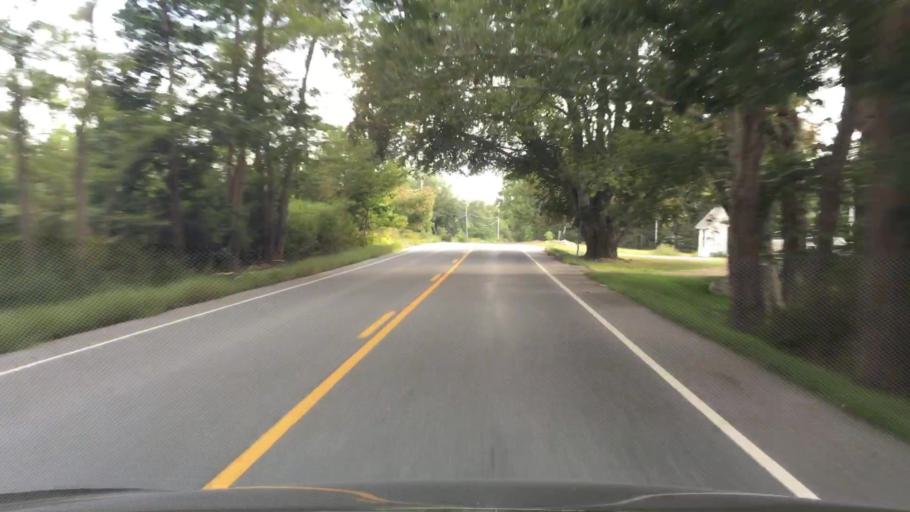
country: US
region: Maine
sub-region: Hancock County
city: Castine
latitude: 44.4385
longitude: -68.7909
